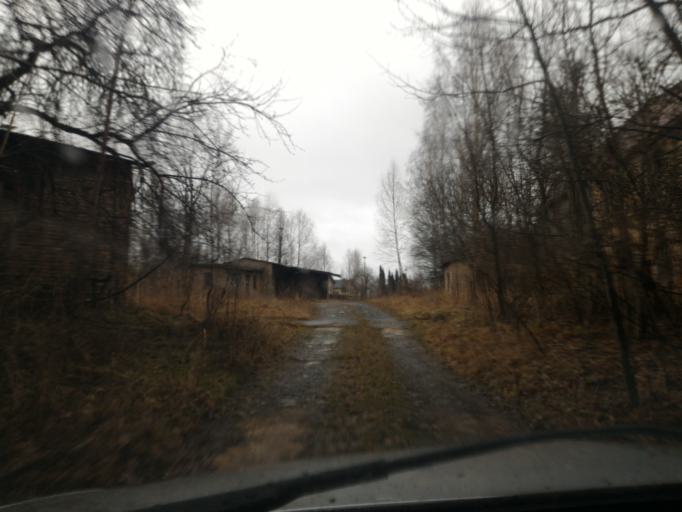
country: DE
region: Saxony
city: Seifhennersdorf
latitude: 50.9374
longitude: 14.6147
